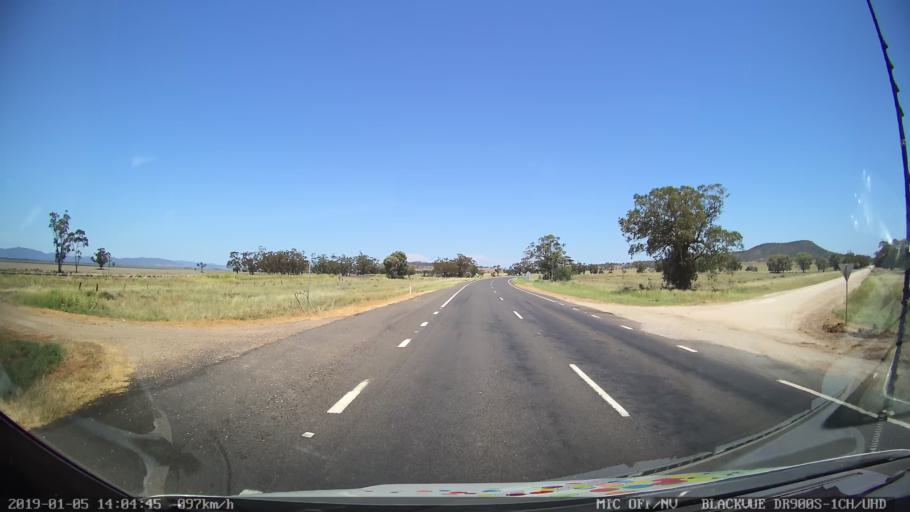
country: AU
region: New South Wales
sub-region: Gunnedah
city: Gunnedah
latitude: -31.2031
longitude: 150.3677
